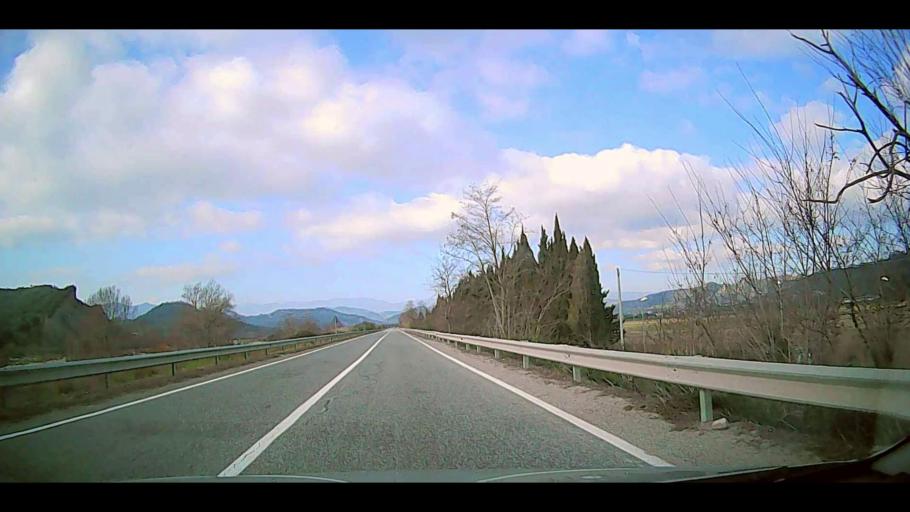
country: IT
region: Calabria
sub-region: Provincia di Crotone
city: Rocca di Neto
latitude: 39.1695
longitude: 16.9803
